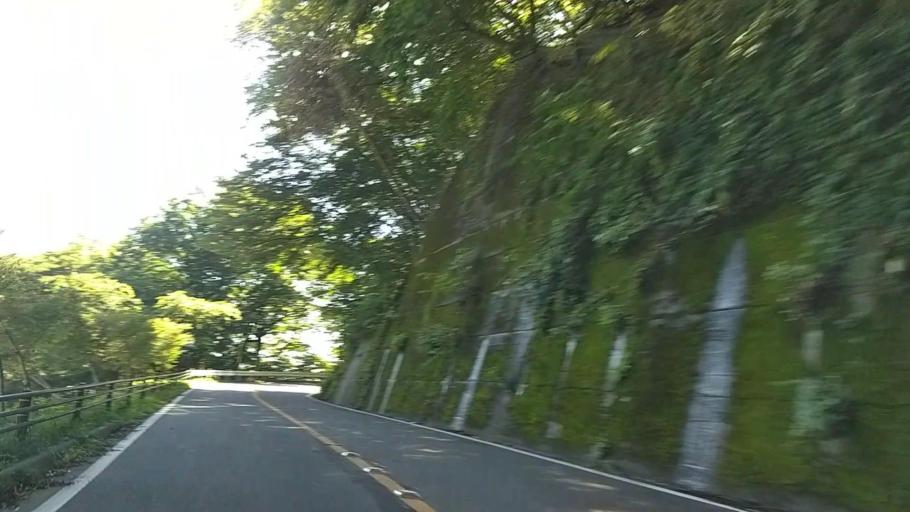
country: JP
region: Gunma
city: Annaka
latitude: 36.3558
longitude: 138.6995
